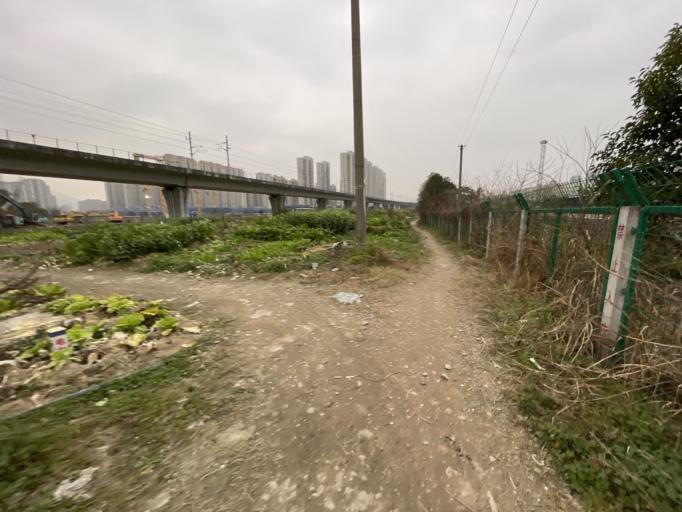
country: CN
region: Zhejiang Sheng
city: Louqiao
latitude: 27.9813
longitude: 120.6223
